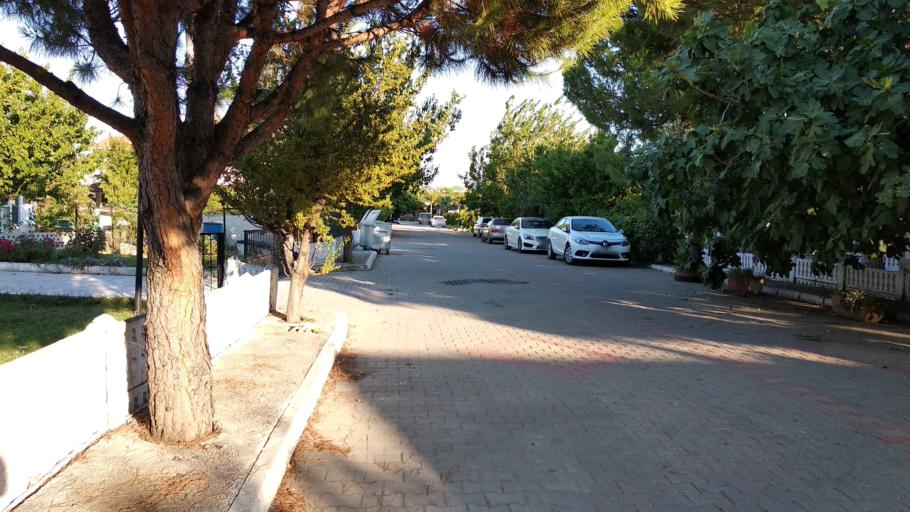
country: TR
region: Balikesir
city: Altinova
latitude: 39.1579
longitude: 26.8204
